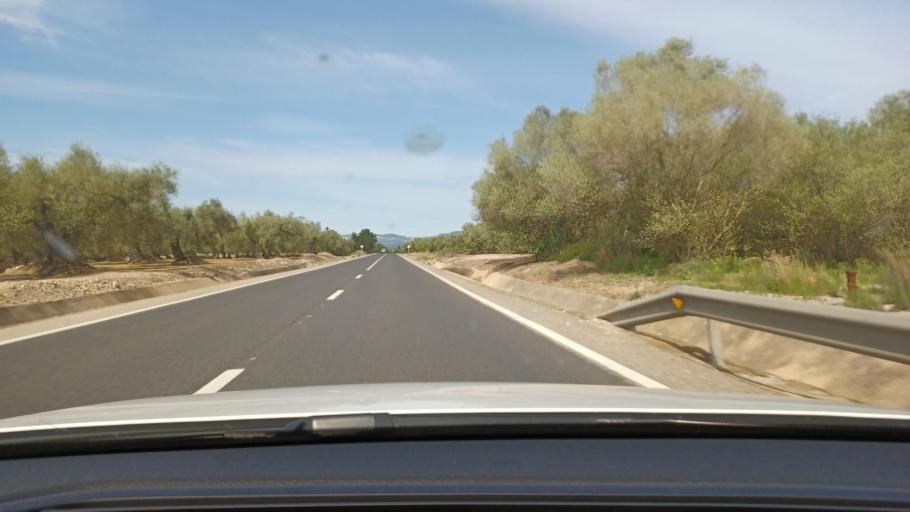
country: ES
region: Catalonia
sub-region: Provincia de Tarragona
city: Mas de Barberans
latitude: 40.6416
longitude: 0.3632
